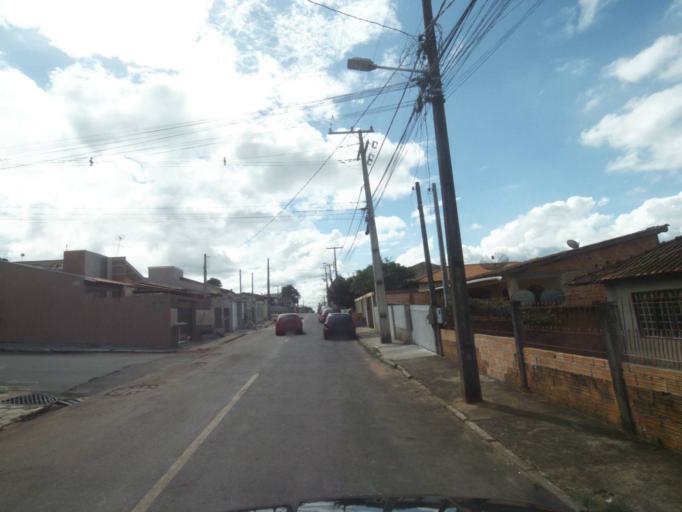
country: BR
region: Parana
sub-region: Telemaco Borba
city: Telemaco Borba
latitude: -24.3167
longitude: -50.6331
